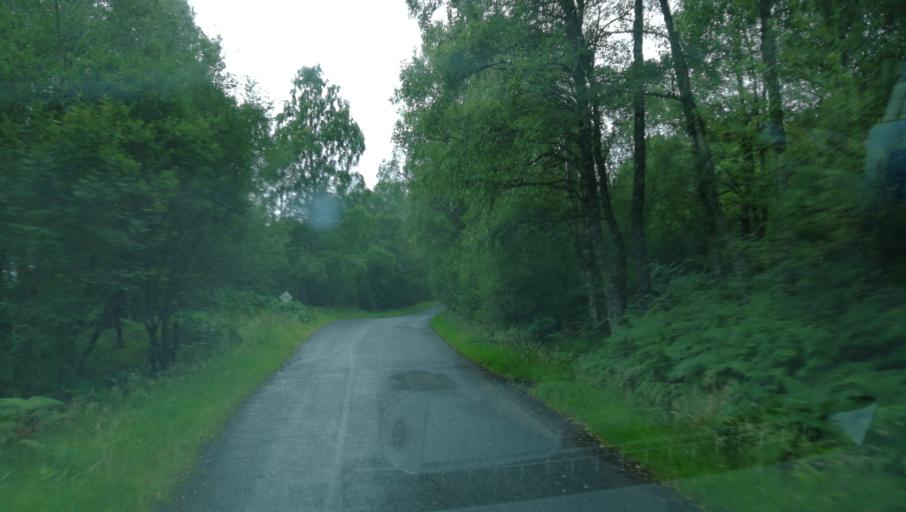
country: GB
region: Scotland
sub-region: Highland
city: Beauly
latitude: 57.3224
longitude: -4.7996
